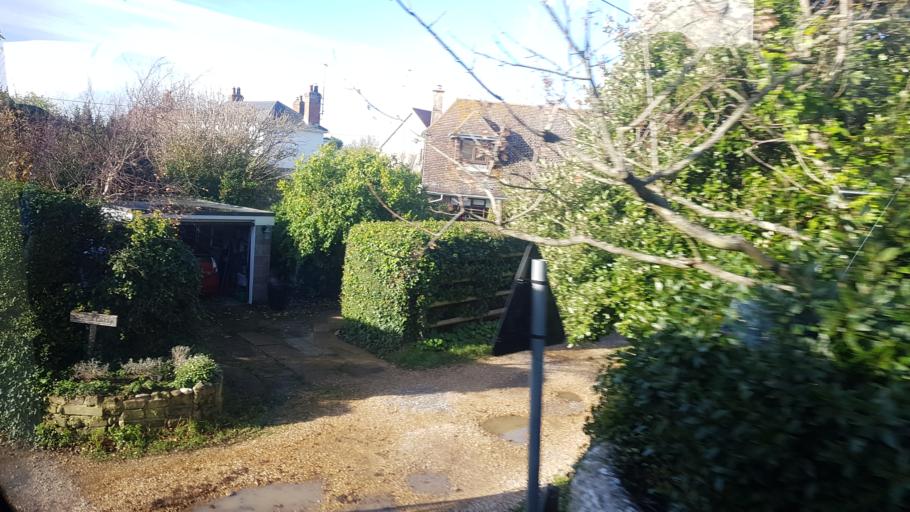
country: GB
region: England
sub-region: Isle of Wight
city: Shalfleet
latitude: 50.6520
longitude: -1.4503
